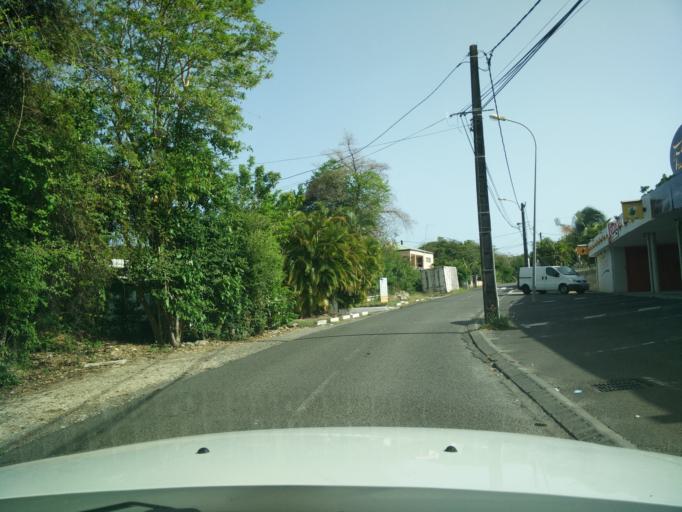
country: GP
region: Guadeloupe
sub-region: Guadeloupe
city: Le Gosier
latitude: 16.2074
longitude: -61.4702
